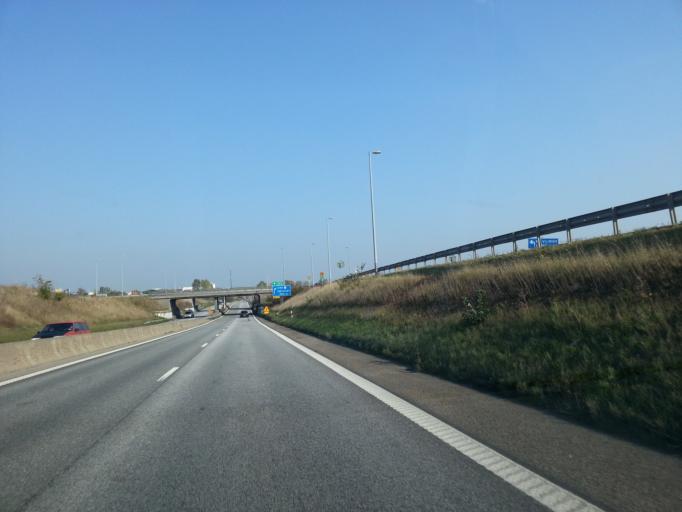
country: SE
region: Skane
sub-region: Lunds Kommun
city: Lund
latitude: 55.6767
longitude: 13.1795
